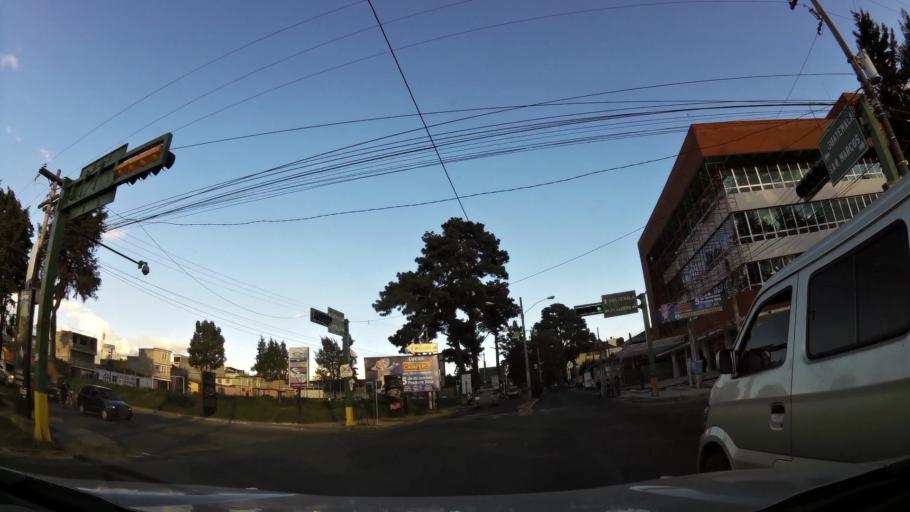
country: GT
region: Quetzaltenango
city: Quetzaltenango
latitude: 14.8453
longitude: -91.5280
